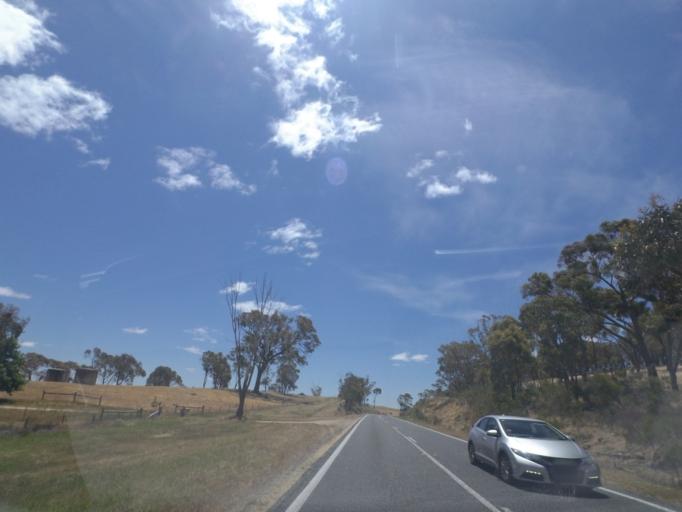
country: AU
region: Victoria
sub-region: Mount Alexander
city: Castlemaine
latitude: -37.2154
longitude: 144.1403
